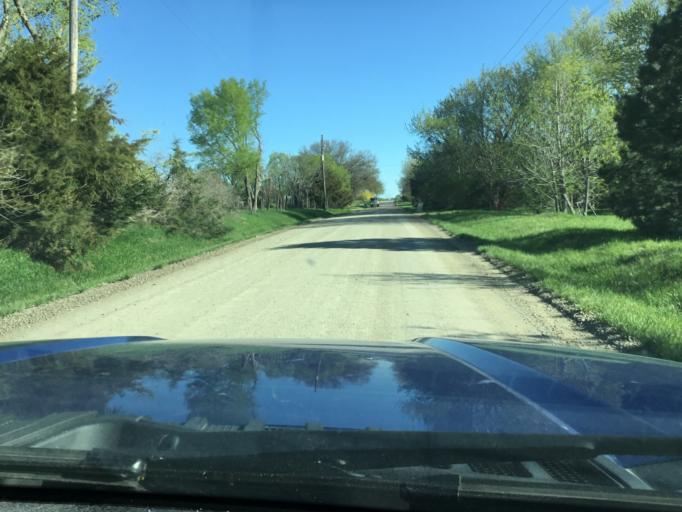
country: US
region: Kansas
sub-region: Douglas County
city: Lawrence
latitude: 38.9772
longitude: -95.3539
